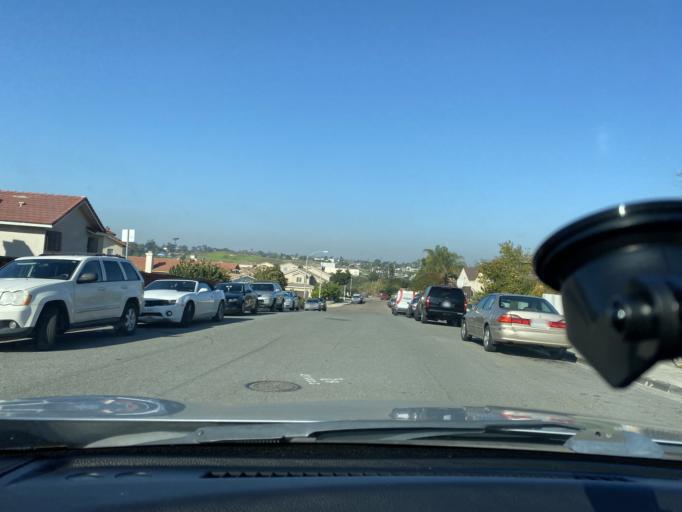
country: US
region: California
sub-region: San Diego County
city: National City
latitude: 32.7052
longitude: -117.0894
